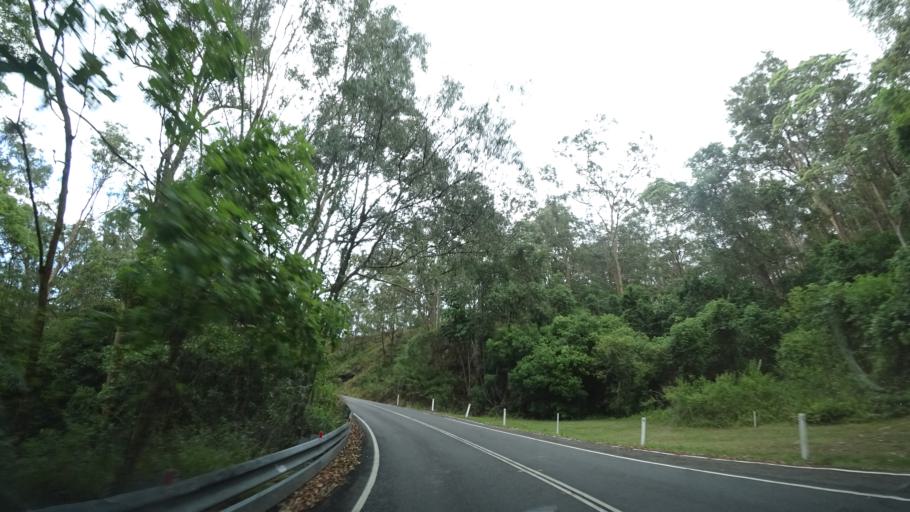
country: AU
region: Queensland
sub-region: Brisbane
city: Taringa
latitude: -27.4640
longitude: 152.9604
